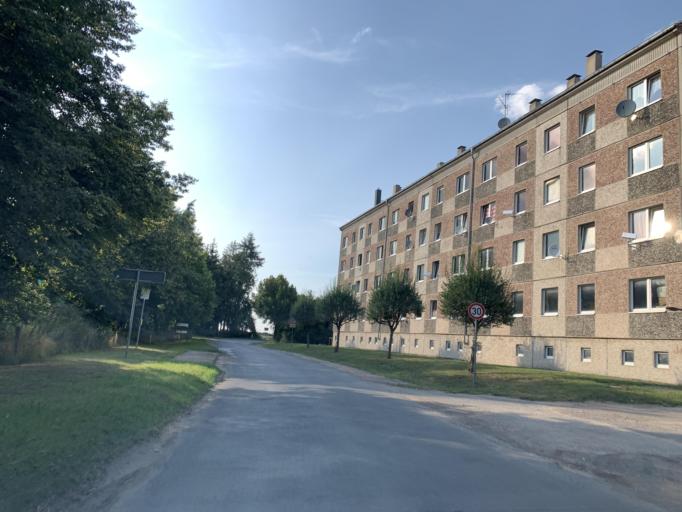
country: DE
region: Mecklenburg-Vorpommern
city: Loitz
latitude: 53.3549
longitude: 13.3544
